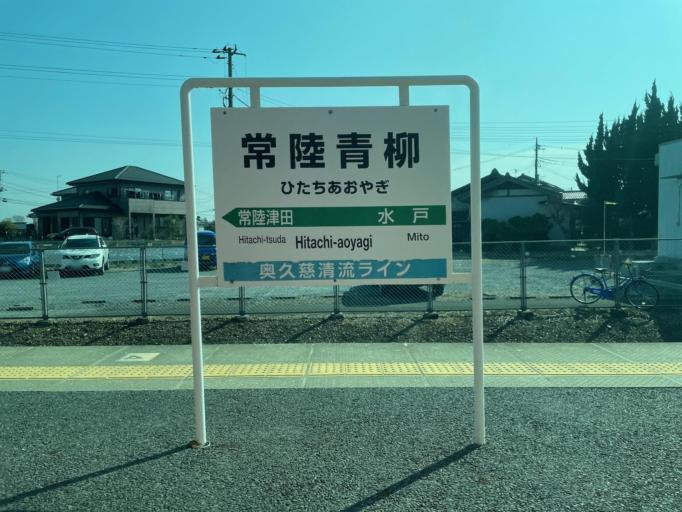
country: JP
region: Ibaraki
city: Katsuta
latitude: 36.3842
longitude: 140.4845
